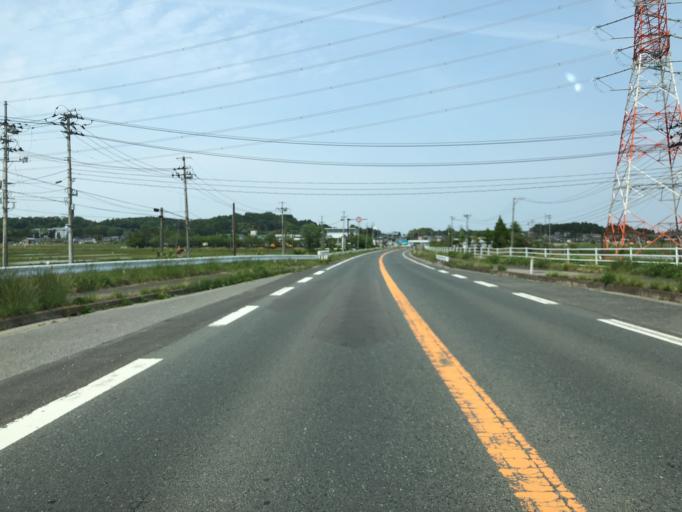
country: JP
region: Miyagi
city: Marumori
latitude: 37.8407
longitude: 140.9182
